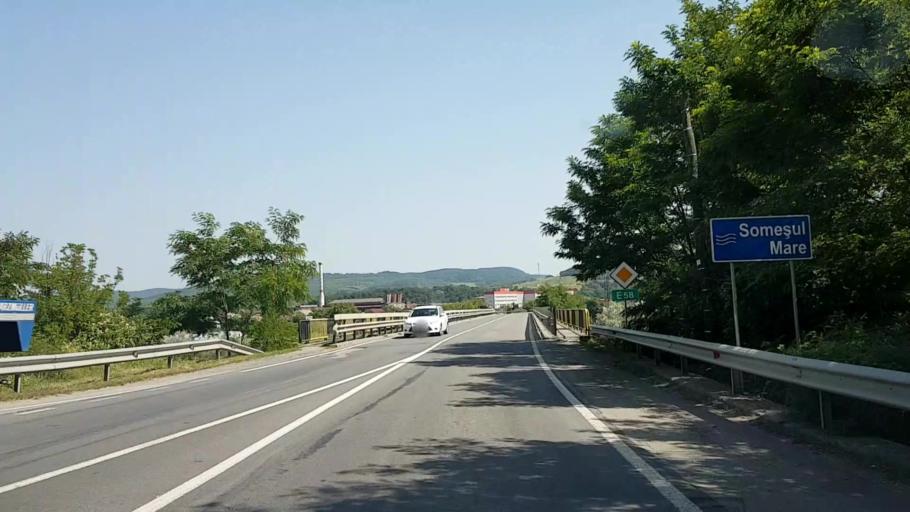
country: RO
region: Bistrita-Nasaud
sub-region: Comuna Beclean
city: Beclean
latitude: 47.1780
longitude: 24.1472
